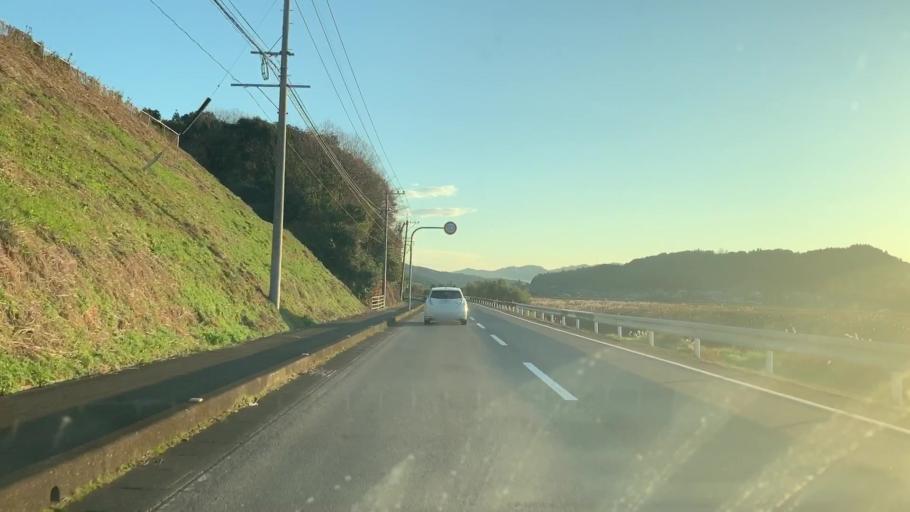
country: JP
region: Saga Prefecture
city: Imaricho-ko
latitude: 33.2775
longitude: 129.9653
